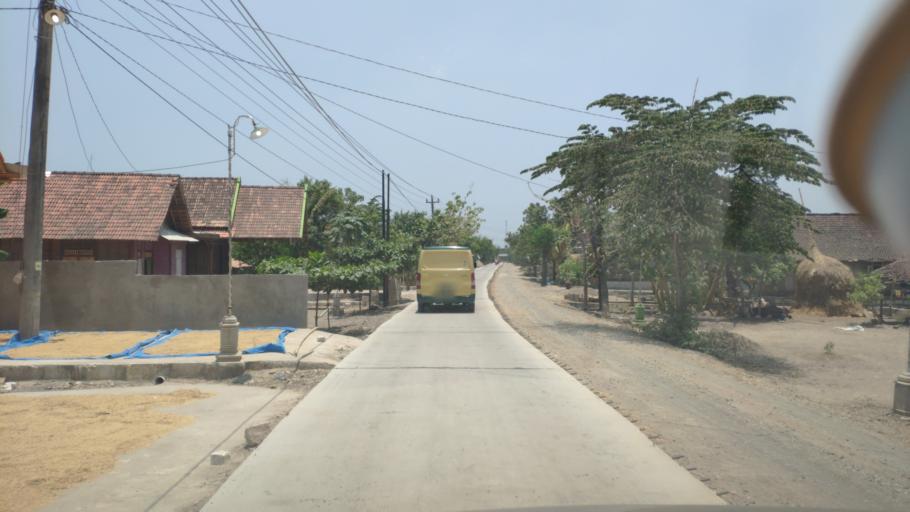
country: ID
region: Central Java
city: Mendenrejo
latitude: -7.2386
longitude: 111.4449
